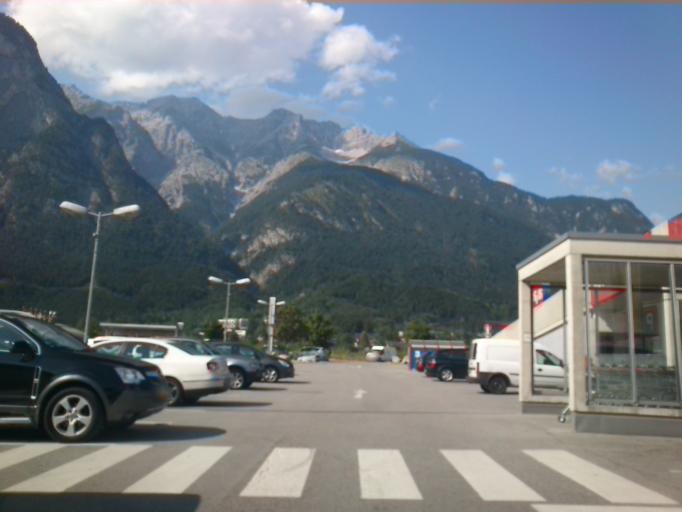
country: AT
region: Tyrol
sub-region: Politischer Bezirk Innsbruck Land
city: Vols
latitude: 47.2565
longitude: 11.3252
